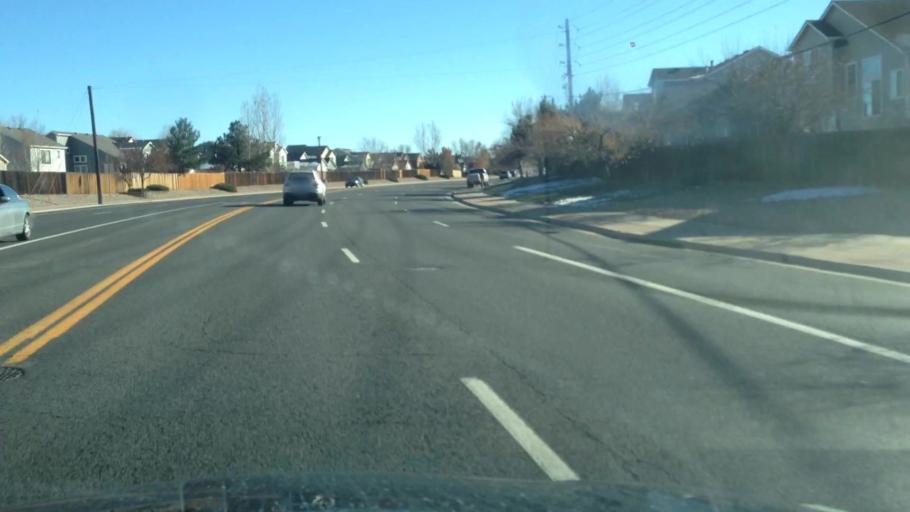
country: US
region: Colorado
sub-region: Douglas County
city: Stonegate
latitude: 39.5595
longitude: -104.7962
